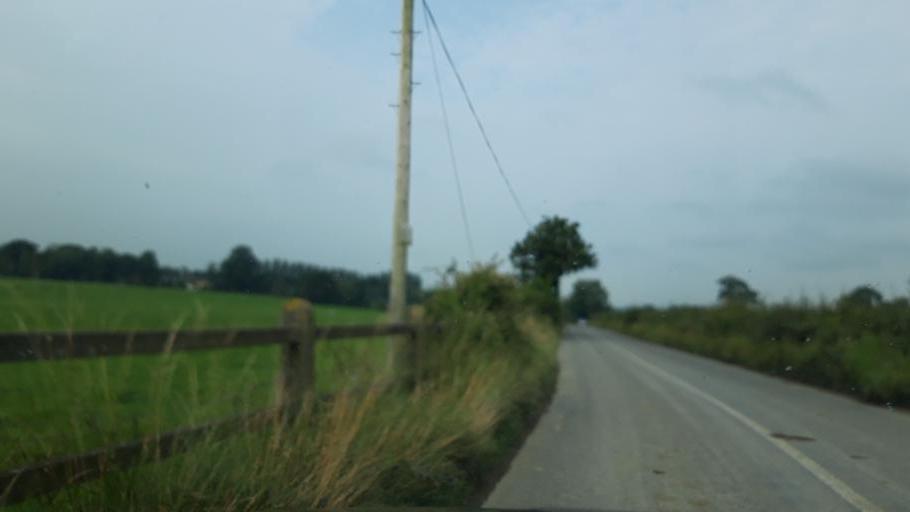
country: IE
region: Munster
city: Fethard
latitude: 52.5567
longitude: -7.5548
